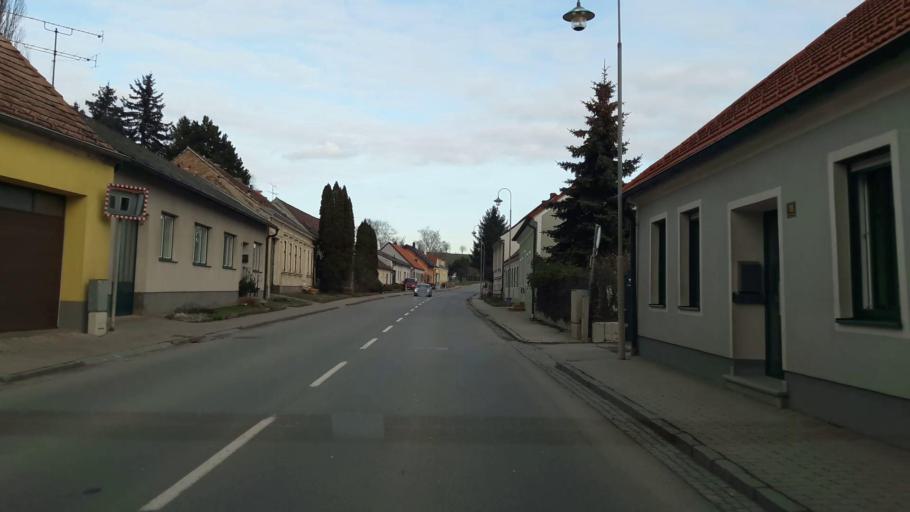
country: AT
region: Lower Austria
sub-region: Politischer Bezirk Mistelbach
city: Asparn an der Zaya
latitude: 48.6292
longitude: 16.5181
